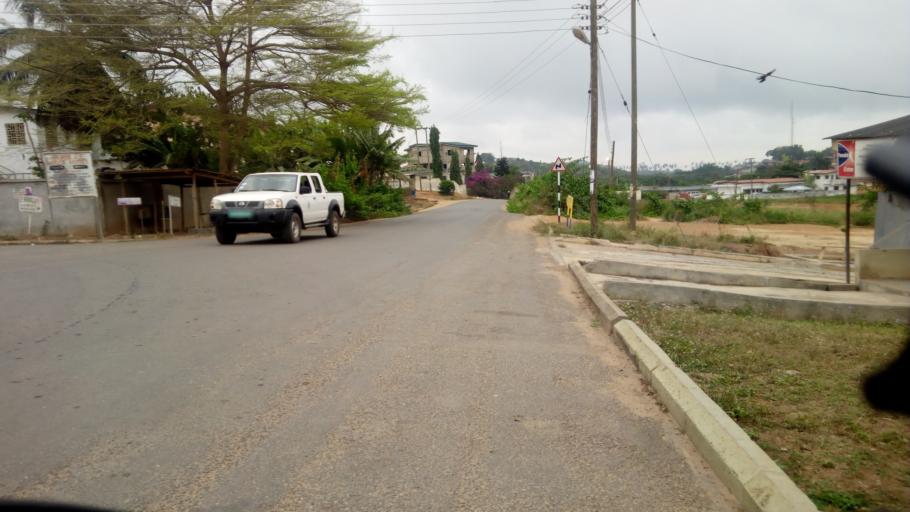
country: GH
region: Central
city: Cape Coast
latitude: 5.1159
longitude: -1.2708
